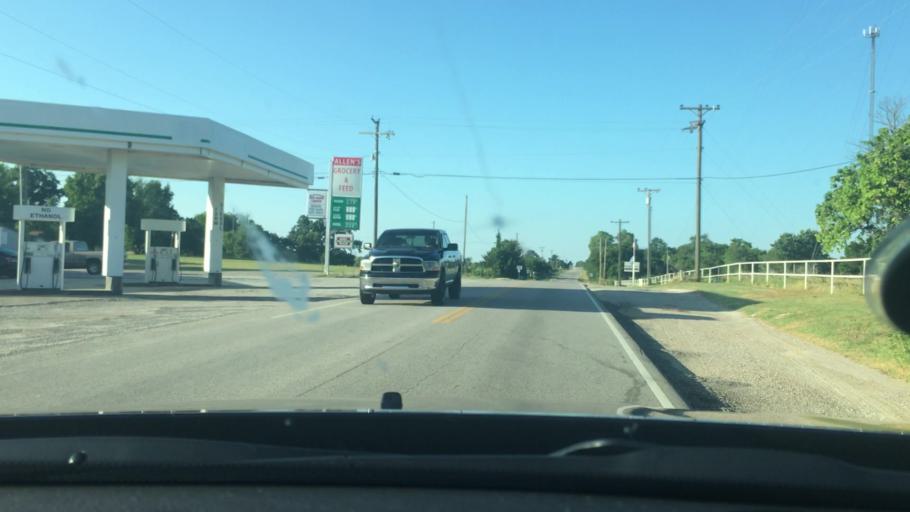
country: US
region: Oklahoma
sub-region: Murray County
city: Sulphur
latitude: 34.6210
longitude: -96.8447
